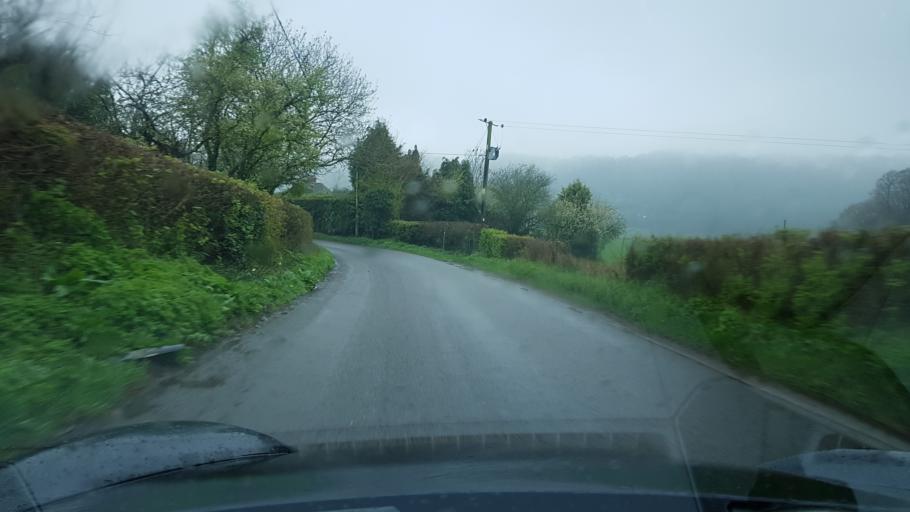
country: GB
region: England
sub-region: Gloucestershire
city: Mitcheldean
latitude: 51.8748
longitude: -2.4866
